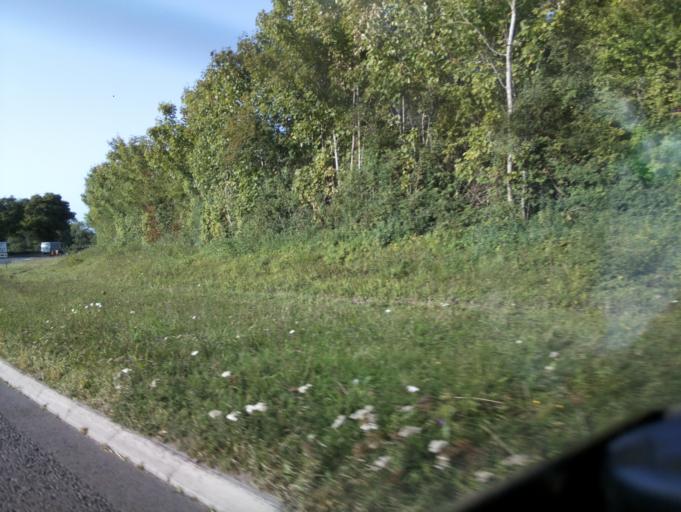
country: GB
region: England
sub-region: Gloucestershire
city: Gloucester
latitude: 51.9074
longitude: -2.2949
